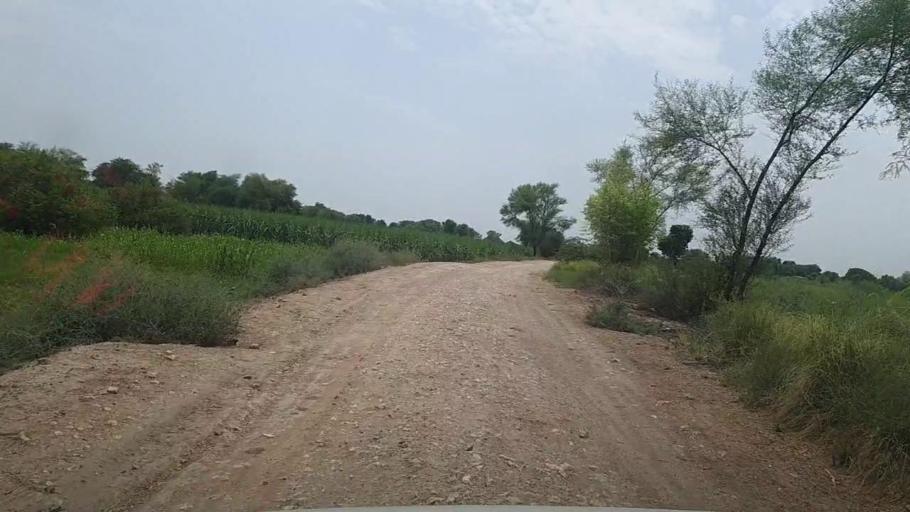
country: PK
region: Sindh
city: Karaundi
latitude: 26.9120
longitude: 68.3224
